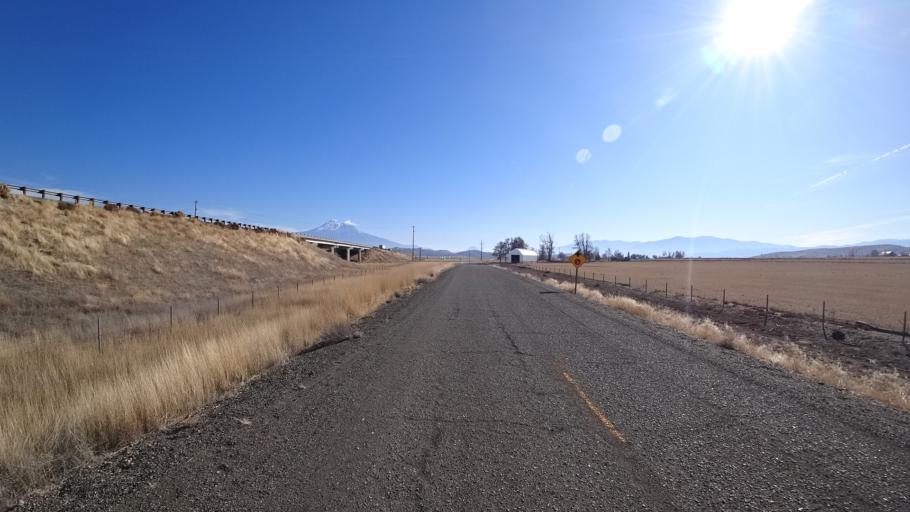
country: US
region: California
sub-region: Siskiyou County
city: Montague
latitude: 41.6284
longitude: -122.5233
